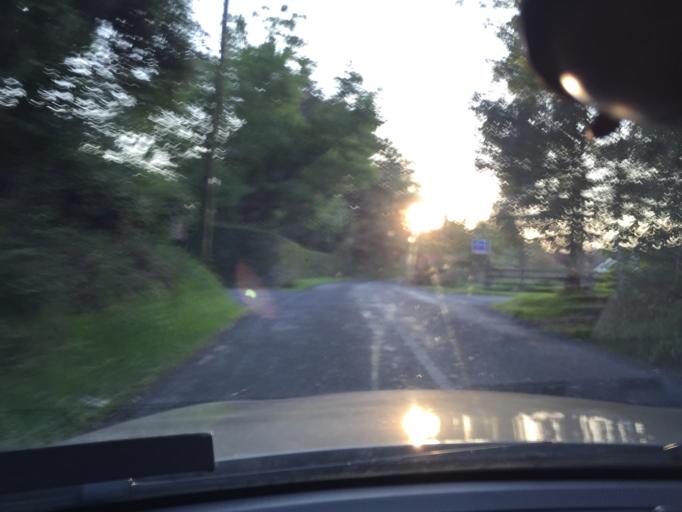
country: IE
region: Leinster
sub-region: Wicklow
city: Enniskerry
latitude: 53.1665
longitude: -6.1719
